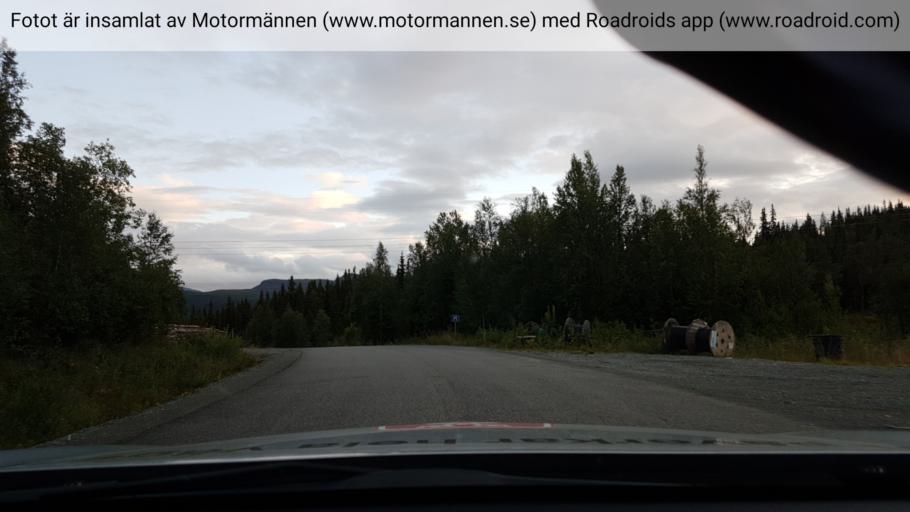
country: SE
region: Vaesterbotten
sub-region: Vilhelmina Kommun
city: Sjoberg
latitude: 65.5069
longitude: 15.6195
